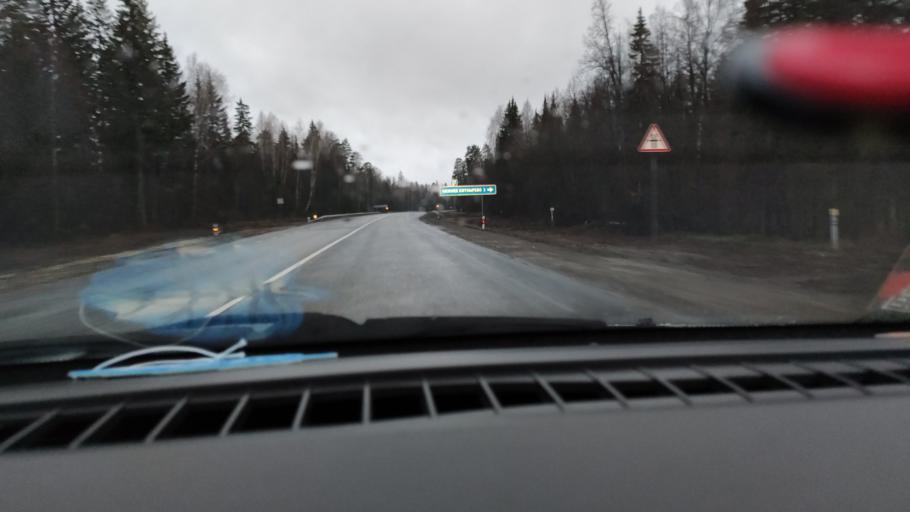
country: RU
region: Udmurtiya
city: Alnashi
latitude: 56.0899
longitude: 52.4424
